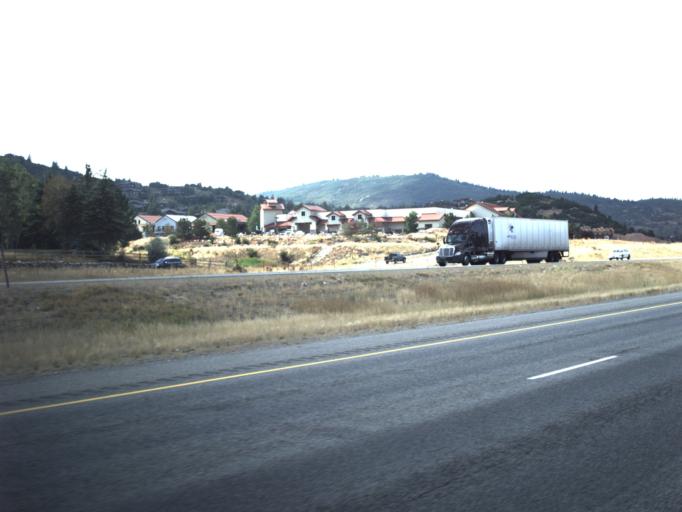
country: US
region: Utah
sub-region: Summit County
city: Summit Park
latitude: 40.7493
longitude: -111.5670
